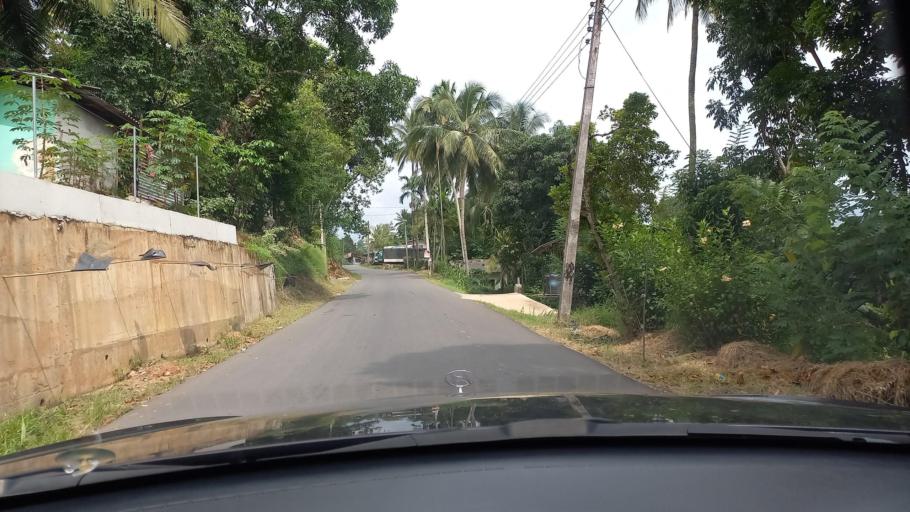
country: LK
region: Central
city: Gampola
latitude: 7.2084
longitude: 80.6209
